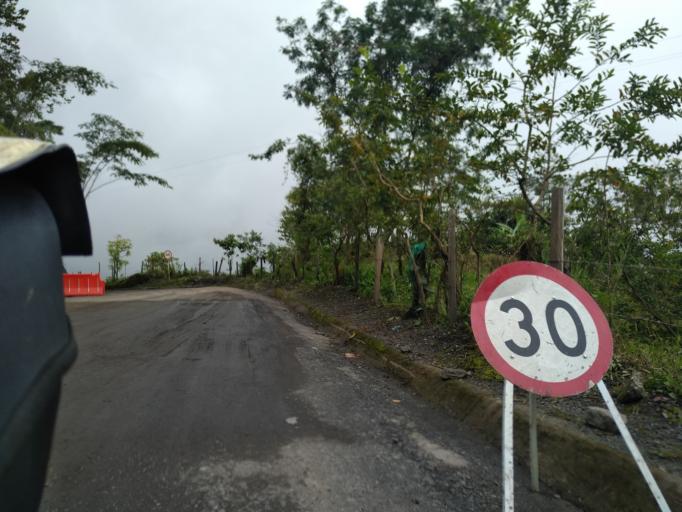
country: CO
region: Santander
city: Landazuri
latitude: 6.1811
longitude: -73.7166
